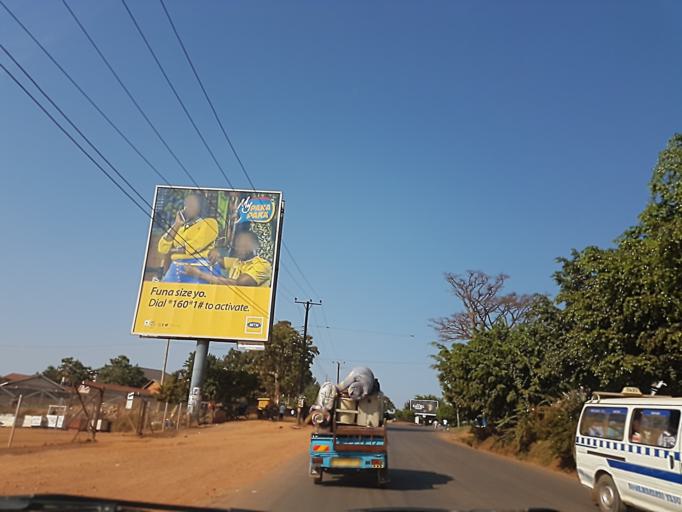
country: UG
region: Central Region
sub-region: Wakiso District
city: Kireka
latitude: 0.3441
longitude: 32.6166
